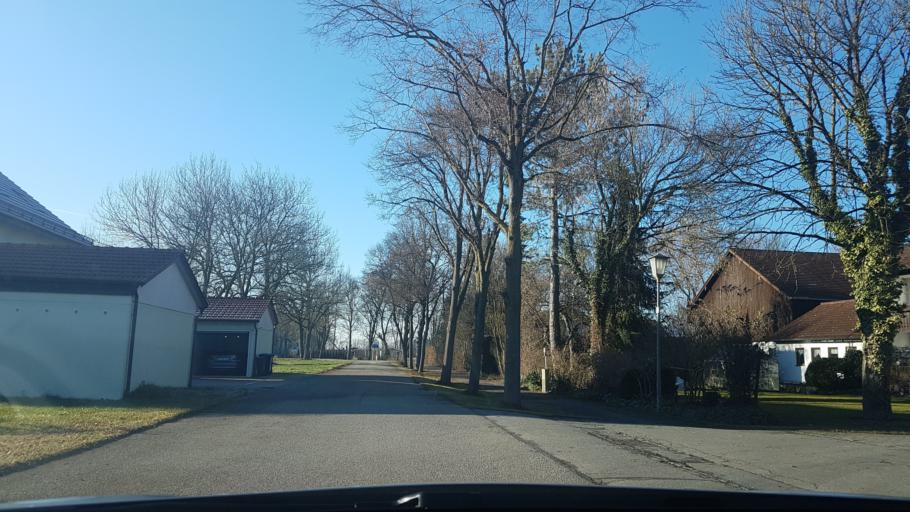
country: DE
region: Bavaria
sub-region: Upper Bavaria
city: Eichenried
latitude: 48.2758
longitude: 11.7496
